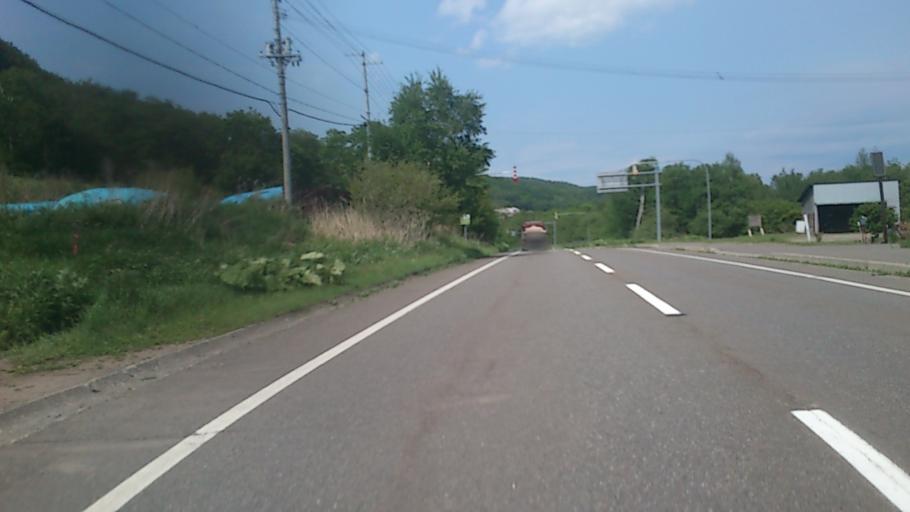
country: JP
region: Hokkaido
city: Otofuke
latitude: 43.2504
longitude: 143.5641
